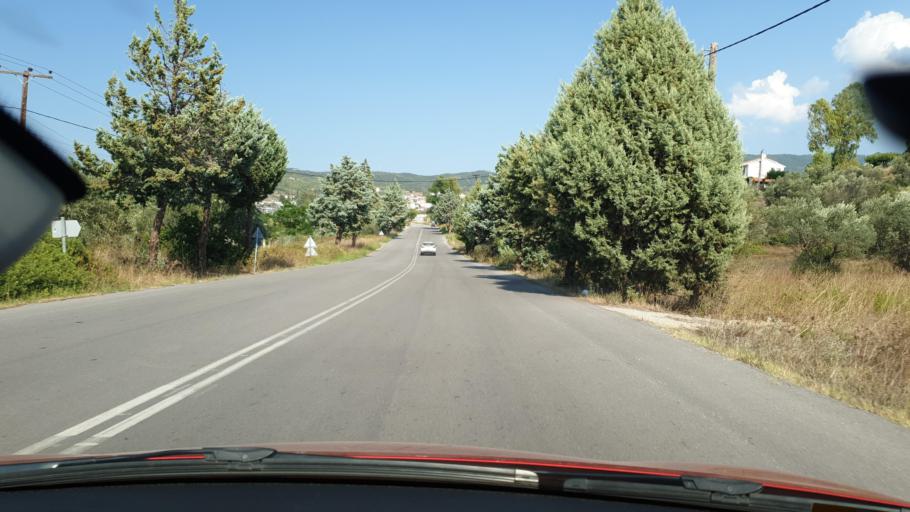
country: GR
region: Central Greece
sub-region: Nomos Evvoias
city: Oreoi
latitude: 38.9016
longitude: 23.0454
